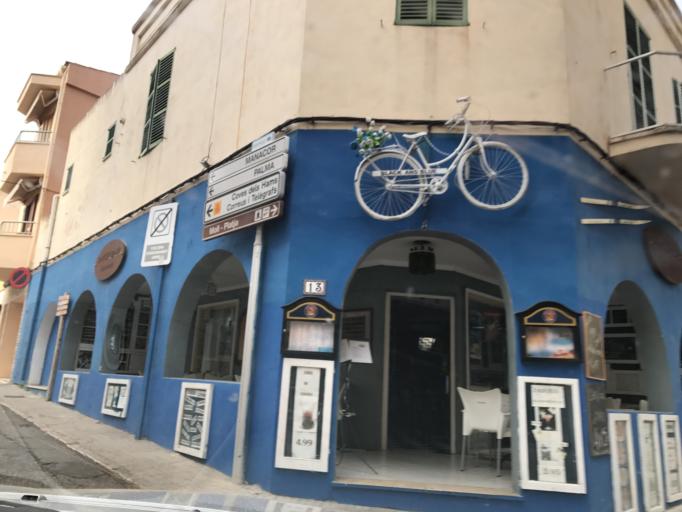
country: ES
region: Balearic Islands
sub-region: Illes Balears
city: Son Servera
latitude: 39.5410
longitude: 3.3334
